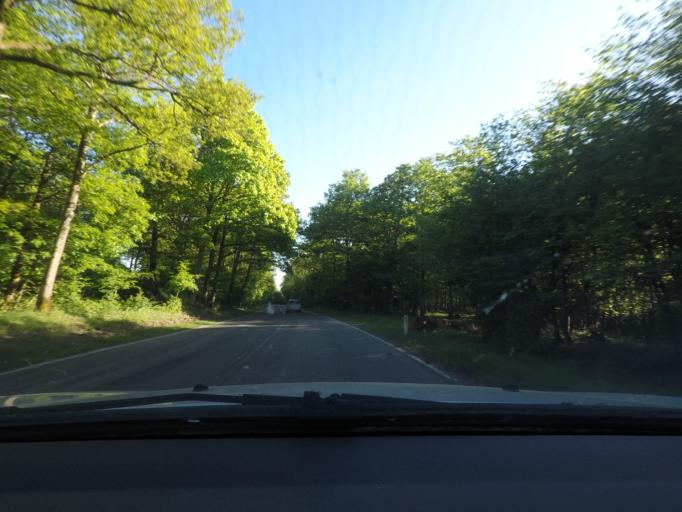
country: BE
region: Wallonia
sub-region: Province de Namur
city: Rochefort
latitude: 50.1960
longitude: 5.1299
